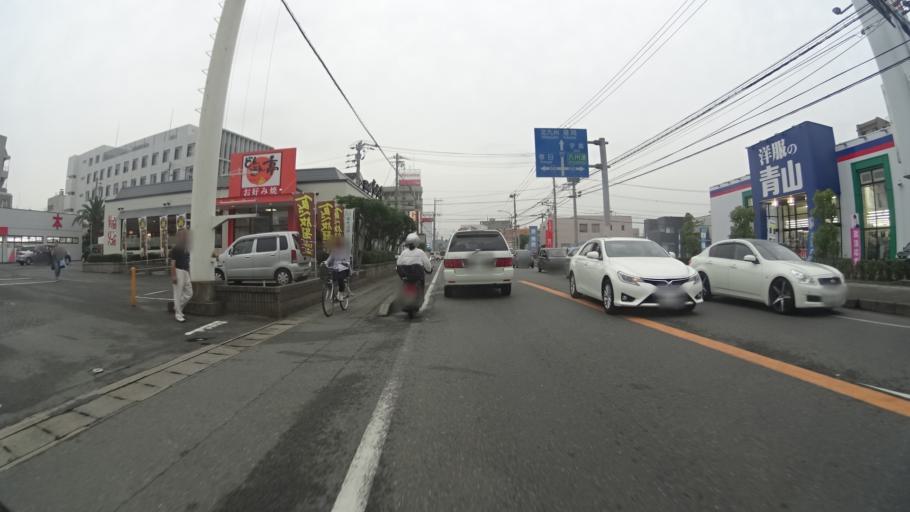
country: JP
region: Fukuoka
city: Onojo
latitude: 33.5309
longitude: 130.4864
